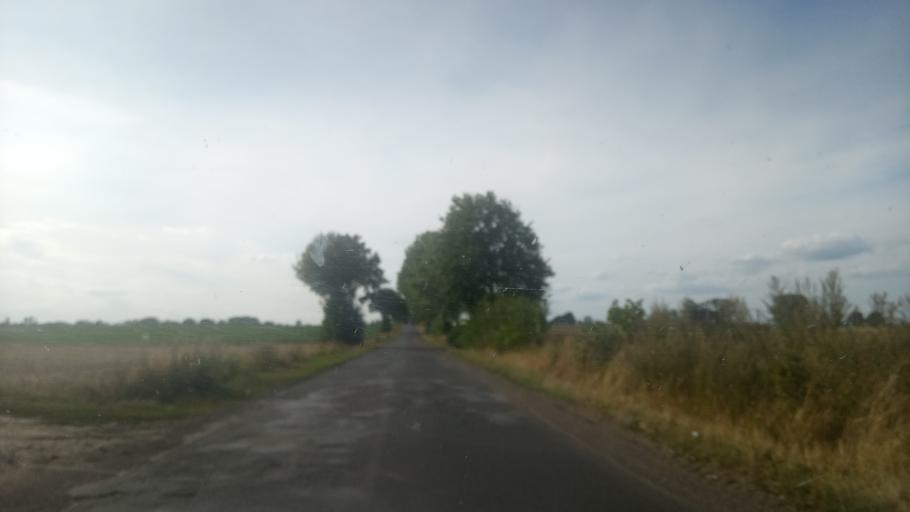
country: PL
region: Kujawsko-Pomorskie
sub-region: Powiat nakielski
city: Sadki
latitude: 53.2047
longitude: 17.3724
